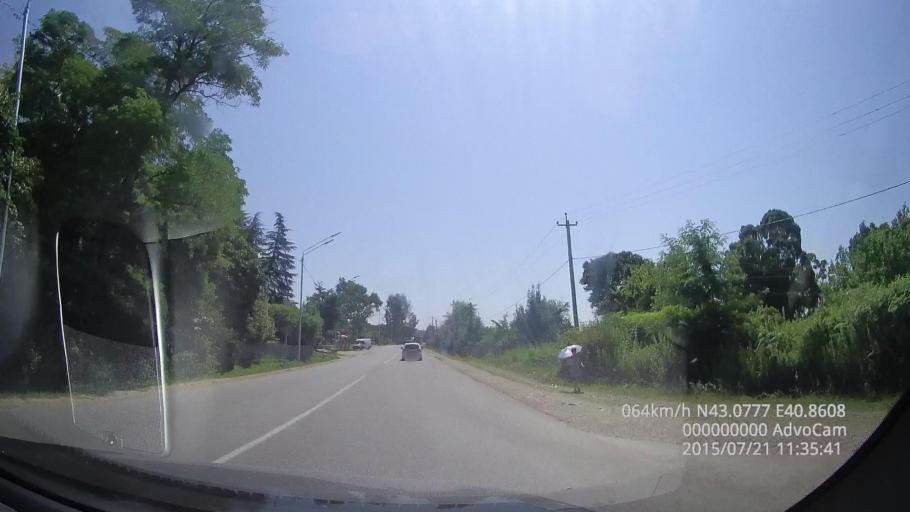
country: GE
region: Abkhazia
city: Stantsiya Novyy Afon
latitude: 43.0776
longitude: 40.8615
